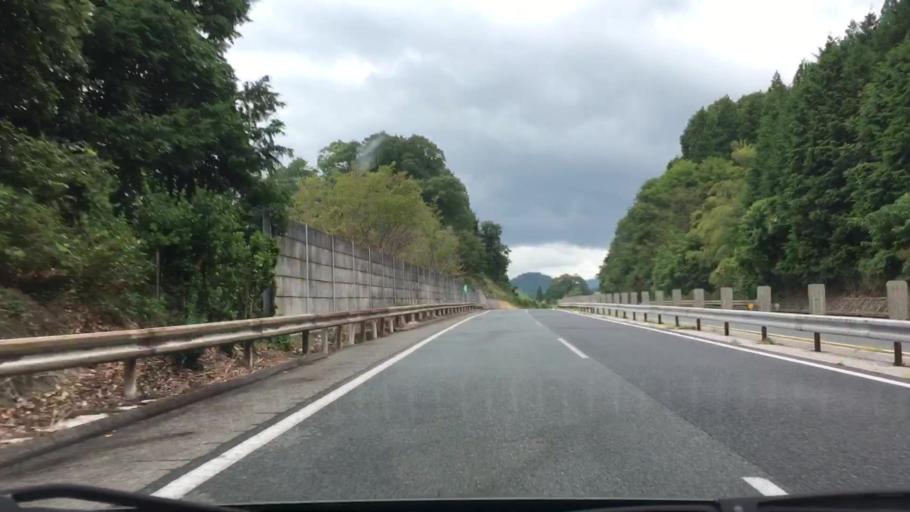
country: JP
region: Okayama
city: Niimi
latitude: 34.9362
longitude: 133.3281
